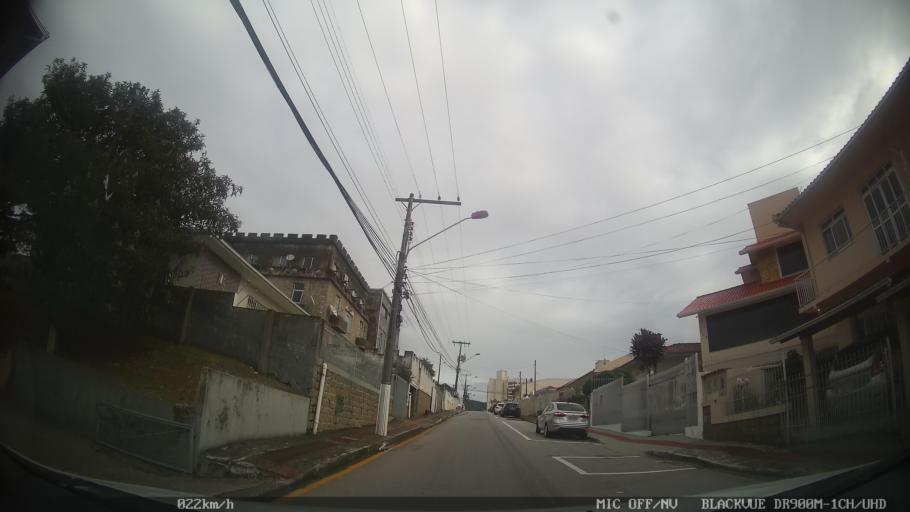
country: BR
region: Santa Catarina
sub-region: Sao Jose
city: Campinas
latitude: -27.5682
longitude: -48.6183
